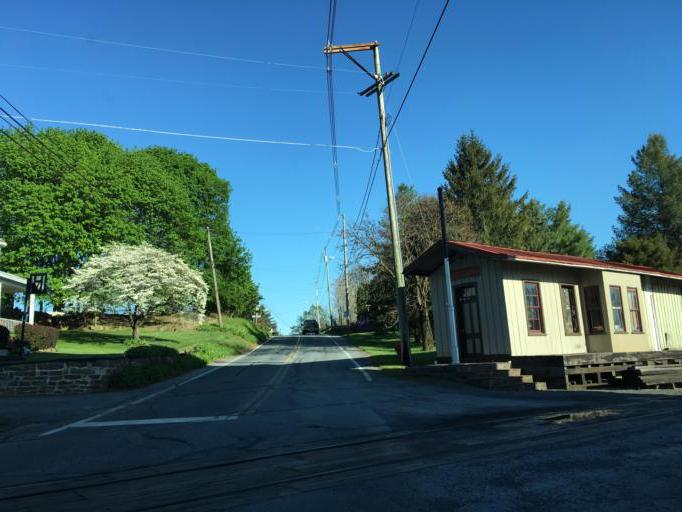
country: US
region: Maryland
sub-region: Frederick County
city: Woodsboro
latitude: 39.5393
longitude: -77.3168
